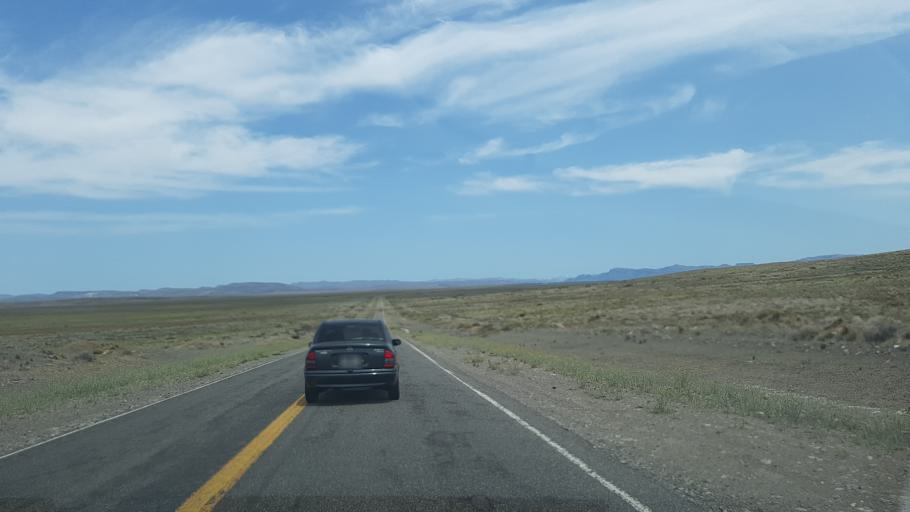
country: AR
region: Rio Negro
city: Pilcaniyeu
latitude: -40.5148
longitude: -70.6892
